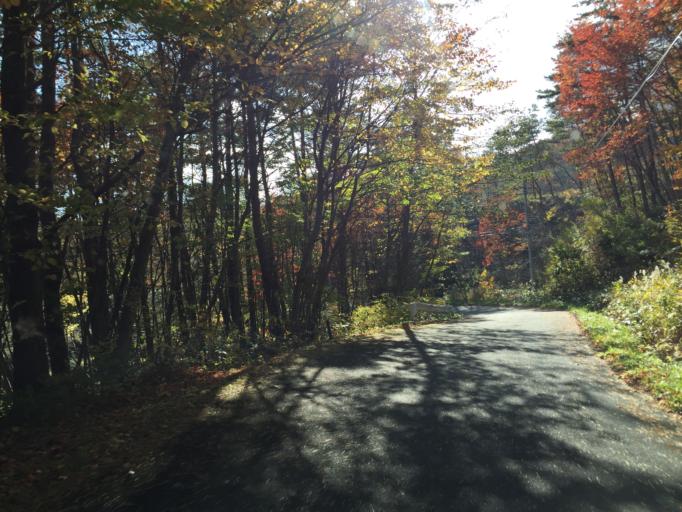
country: JP
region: Fukushima
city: Fukushima-shi
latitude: 37.7252
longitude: 140.3122
